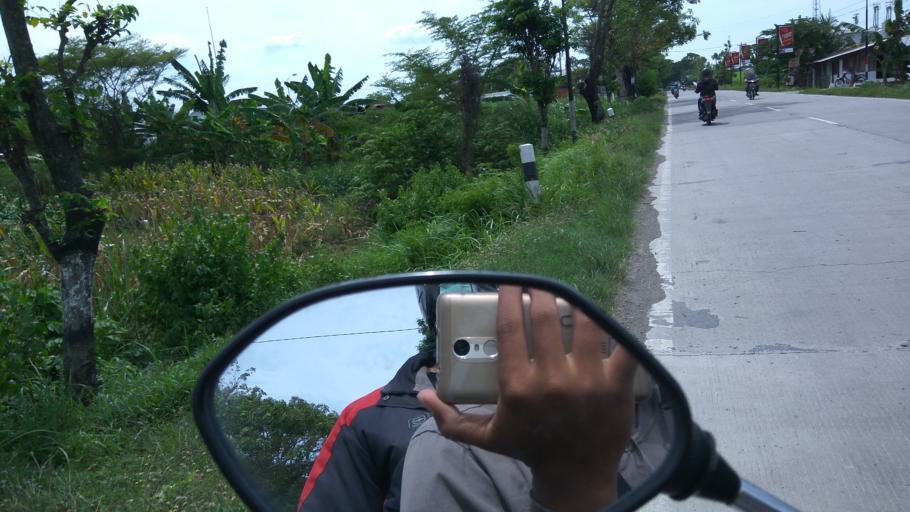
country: ID
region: Central Java
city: Mranggen
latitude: -7.0471
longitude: 110.5876
